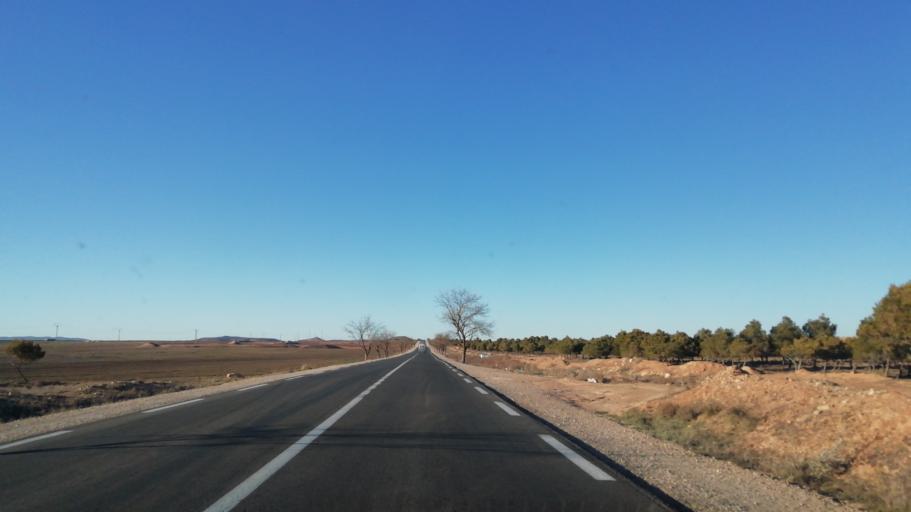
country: DZ
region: Tlemcen
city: Sebdou
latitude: 34.5310
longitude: -1.2953
